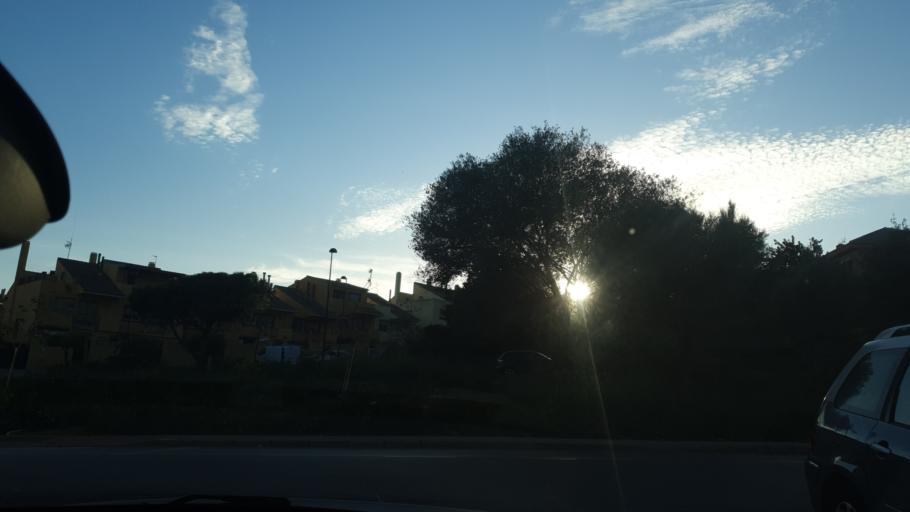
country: ES
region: Andalusia
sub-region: Provincia de Malaga
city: Marbella
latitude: 36.5247
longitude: -4.8958
